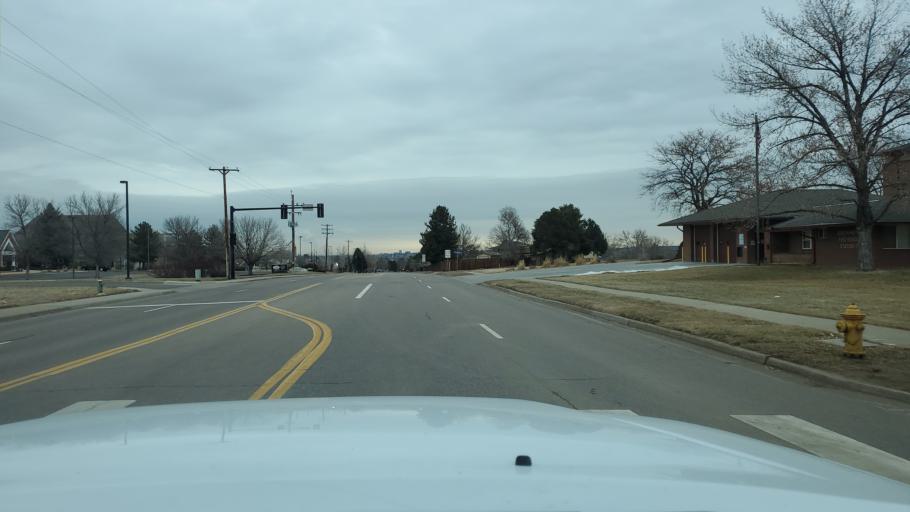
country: US
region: Colorado
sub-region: Arapahoe County
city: Southglenn
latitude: 39.5968
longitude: -104.9414
